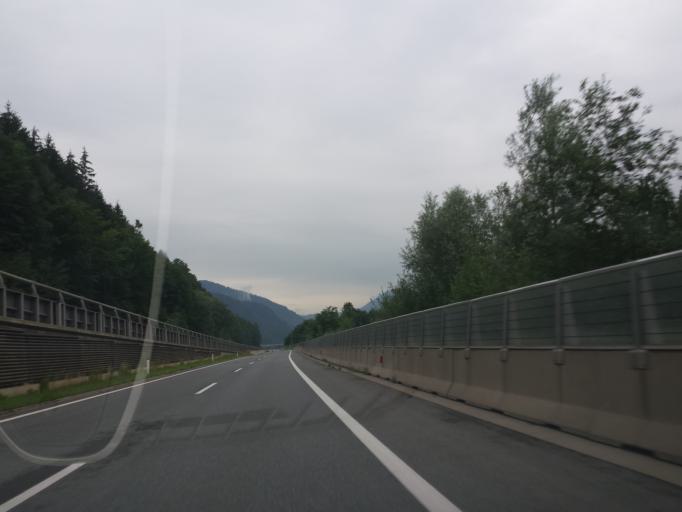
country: AT
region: Styria
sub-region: Politischer Bezirk Graz-Umgebung
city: Rothelstein
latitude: 47.3210
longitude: 15.3659
